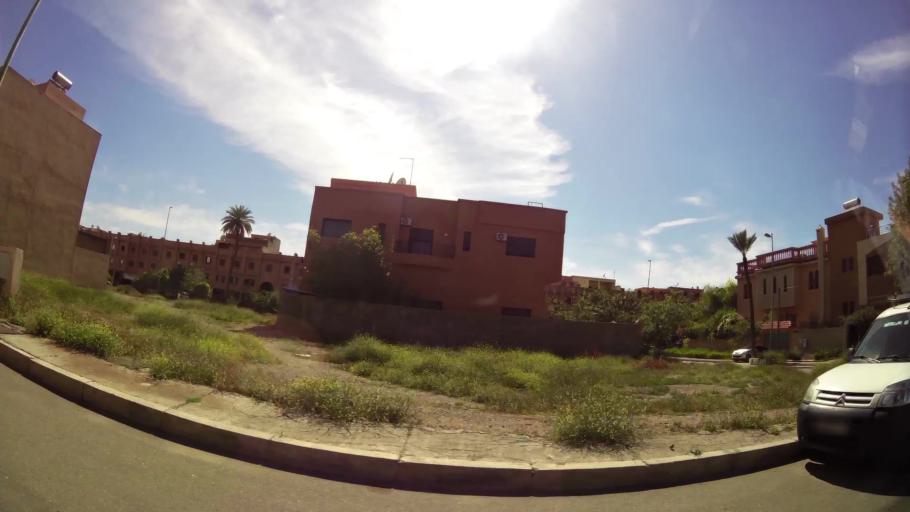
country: MA
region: Marrakech-Tensift-Al Haouz
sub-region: Marrakech
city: Marrakesh
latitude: 31.6369
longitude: -8.0419
